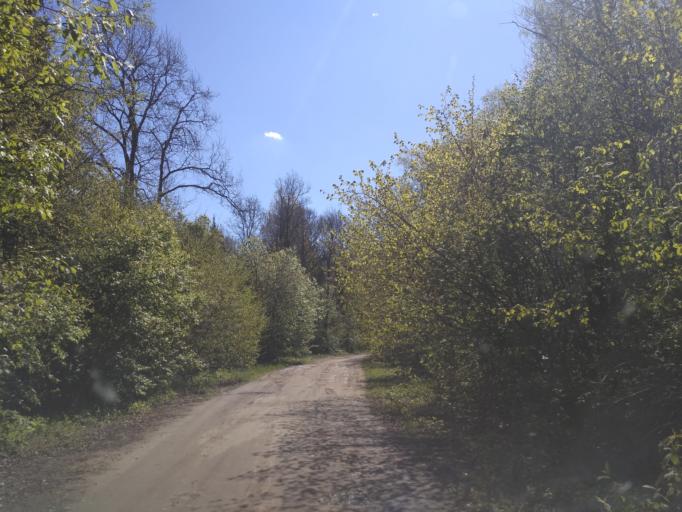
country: BY
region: Mogilev
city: Mstsislaw
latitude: 54.0486
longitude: 31.6965
